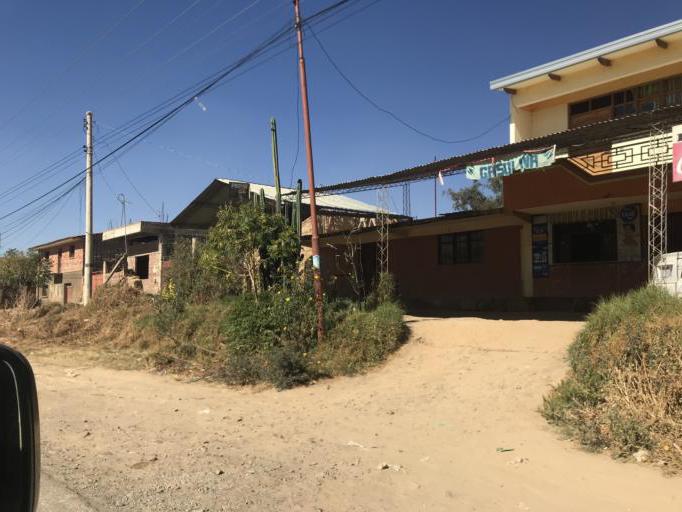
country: BO
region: Cochabamba
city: Cliza
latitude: -17.5765
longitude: -65.9058
